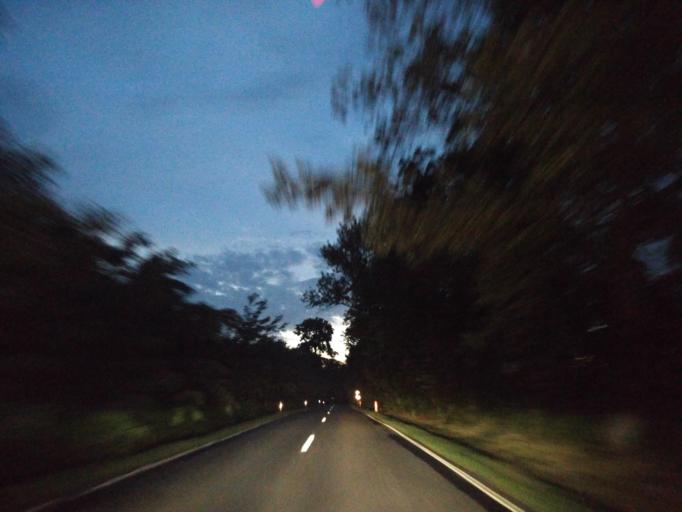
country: HU
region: Fejer
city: Bicske
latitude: 47.4060
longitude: 18.5848
